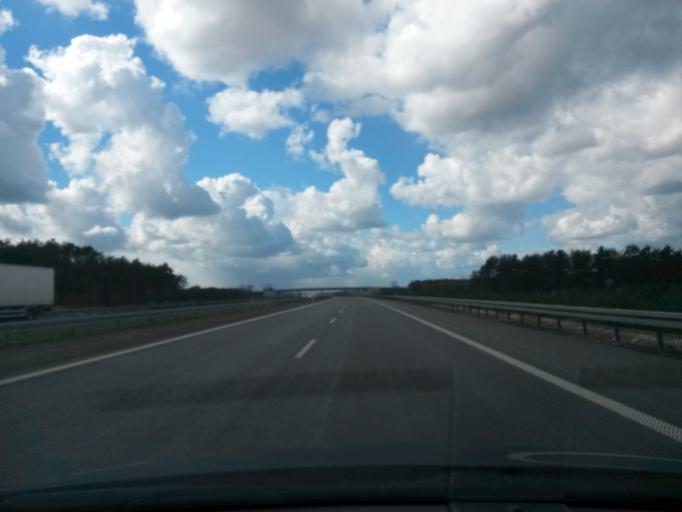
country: PL
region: Greater Poland Voivodeship
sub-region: Powiat kolski
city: Grzegorzew
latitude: 52.1178
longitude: 18.7206
